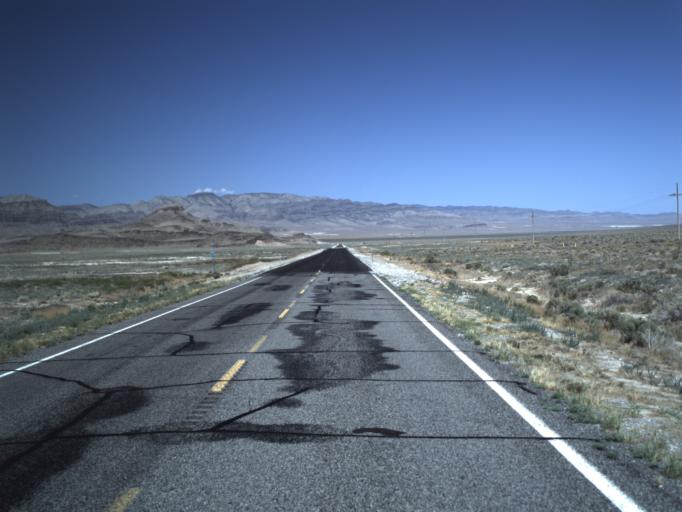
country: US
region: Utah
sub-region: Beaver County
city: Milford
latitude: 39.0472
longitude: -113.4131
